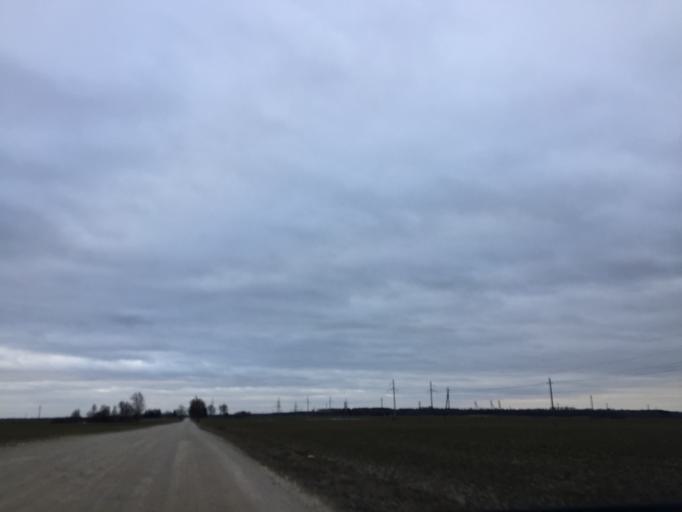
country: LT
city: Zagare
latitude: 56.3438
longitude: 23.2507
